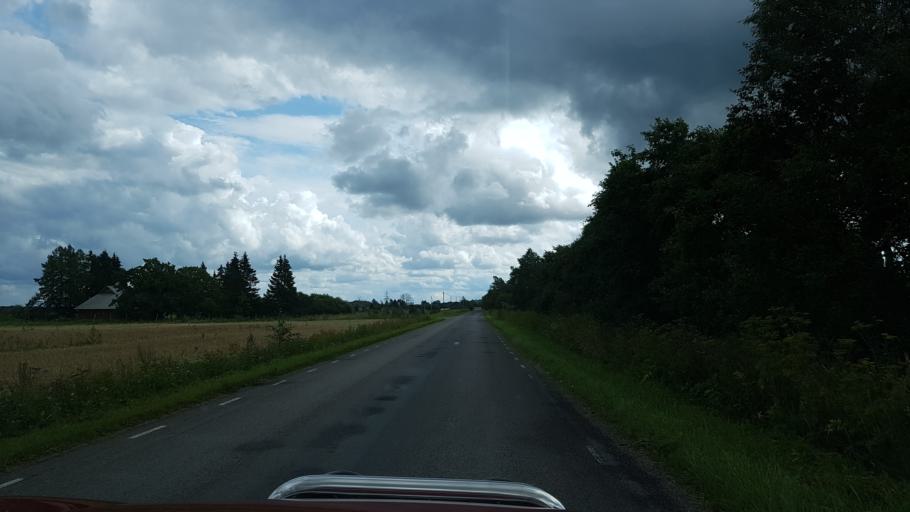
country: EE
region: Laeaene
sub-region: Lihula vald
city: Lihula
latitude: 58.7191
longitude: 23.9813
